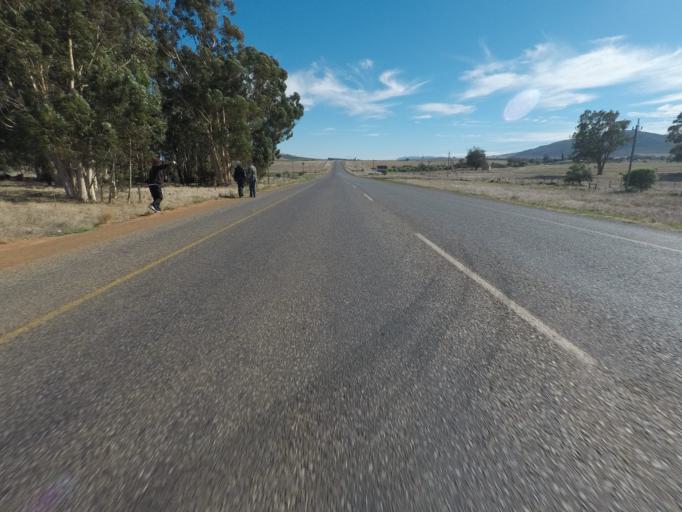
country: ZA
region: Western Cape
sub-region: West Coast District Municipality
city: Malmesbury
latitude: -33.6160
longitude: 18.7269
